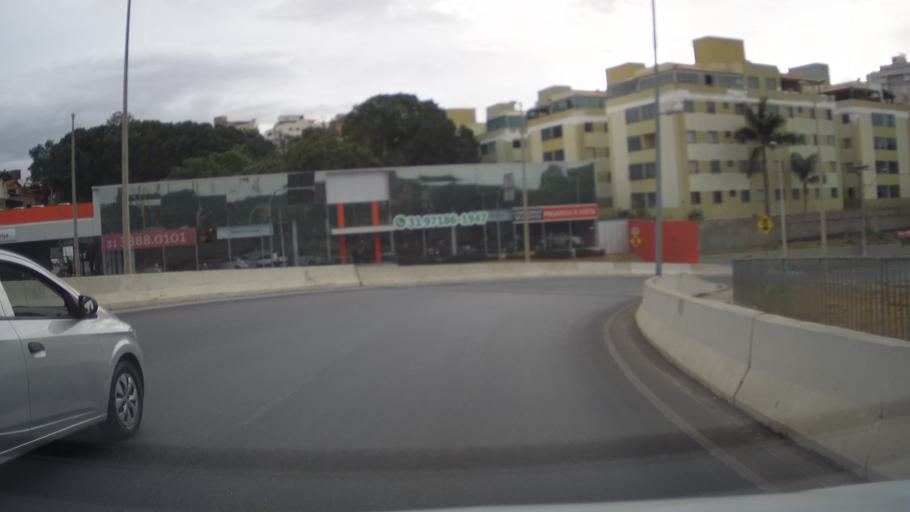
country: BR
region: Minas Gerais
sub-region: Belo Horizonte
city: Belo Horizonte
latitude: -19.8603
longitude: -43.9587
